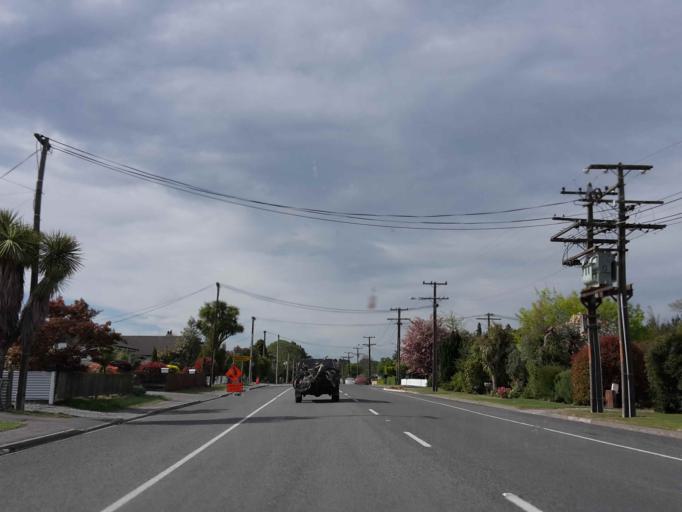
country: NZ
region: Canterbury
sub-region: Timaru District
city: Pleasant Point
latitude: -44.1014
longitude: 171.2381
